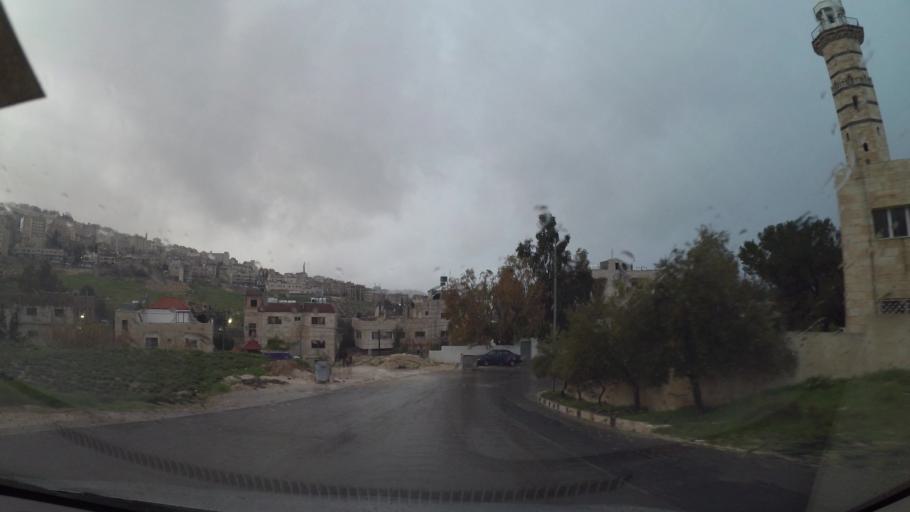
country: JO
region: Amman
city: Al Jubayhah
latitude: 32.0305
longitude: 35.8421
